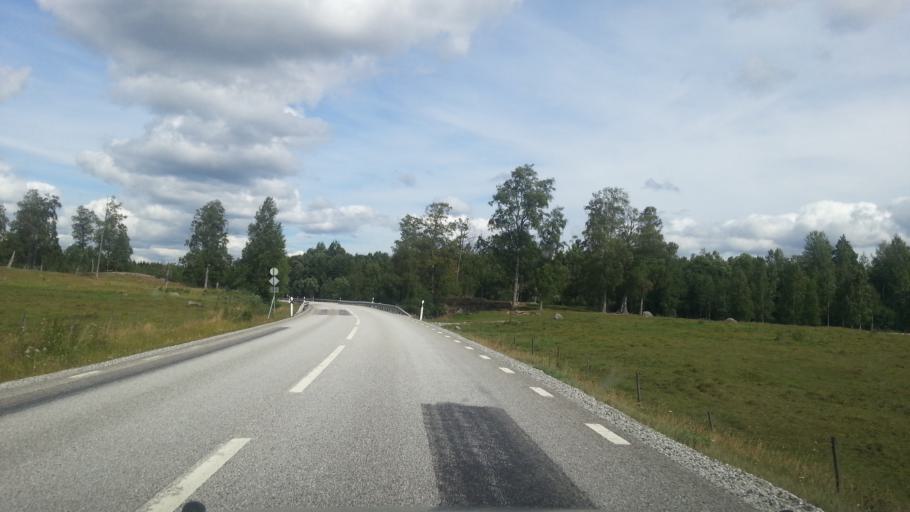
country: SE
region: Vaestmanland
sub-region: Skinnskattebergs Kommun
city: Skinnskatteberg
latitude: 59.7755
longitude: 15.5428
